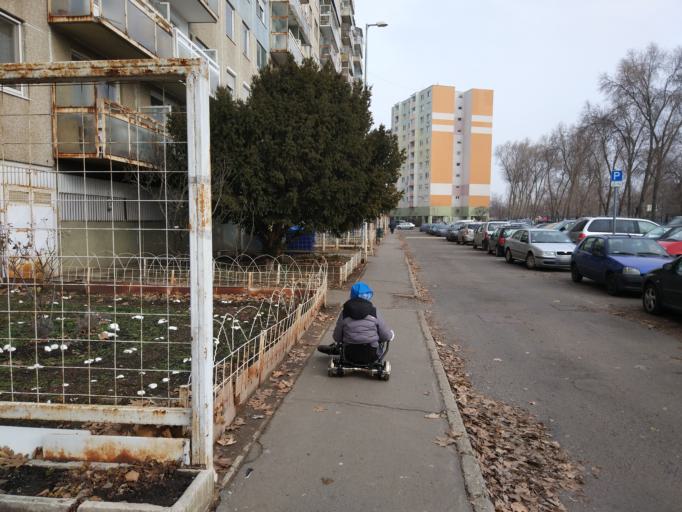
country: HU
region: Budapest
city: Budapest XVIII. keruelet
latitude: 47.4346
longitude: 19.1661
